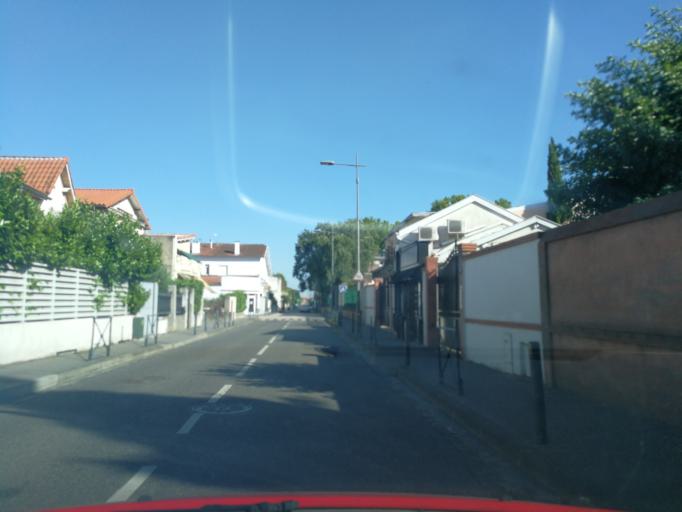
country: FR
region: Midi-Pyrenees
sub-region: Departement de la Haute-Garonne
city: Balma
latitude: 43.6180
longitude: 1.4711
